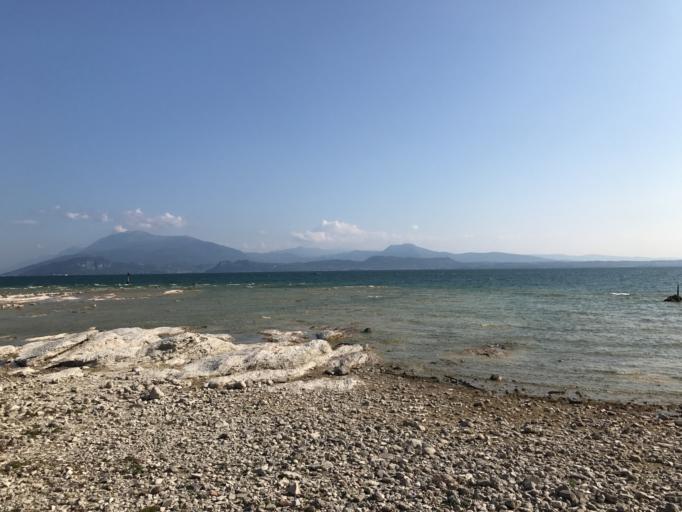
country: IT
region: Lombardy
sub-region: Provincia di Brescia
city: Sirmione
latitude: 45.4974
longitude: 10.6080
